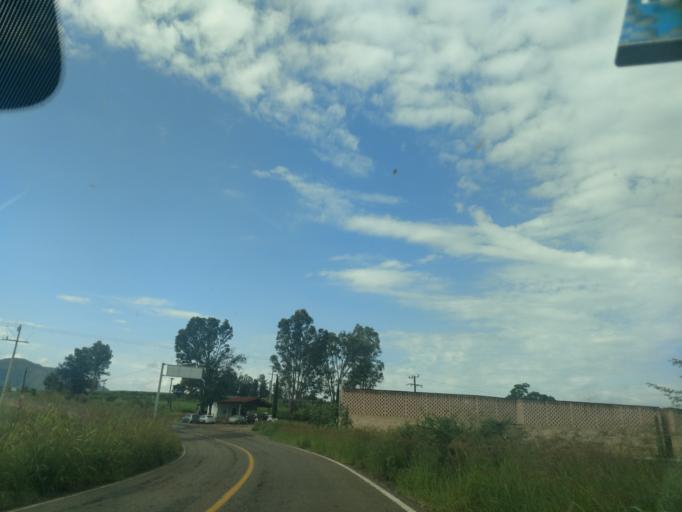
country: MX
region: Jalisco
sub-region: Atengo
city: Soyatlan del Oro
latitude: 20.5245
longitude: -104.3374
